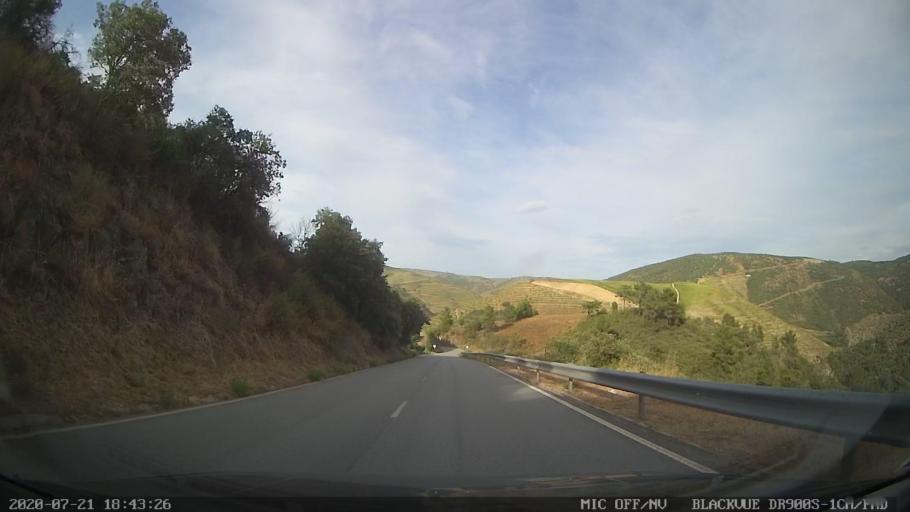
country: PT
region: Viseu
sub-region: Sao Joao da Pesqueira
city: Sao Joao da Pesqueira
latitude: 41.1129
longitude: -7.4587
